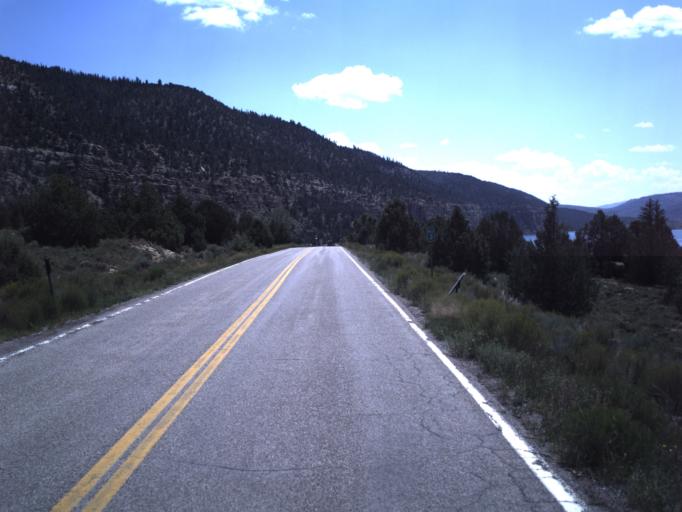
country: US
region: Utah
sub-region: Emery County
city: Orangeville
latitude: 39.3129
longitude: -111.2752
